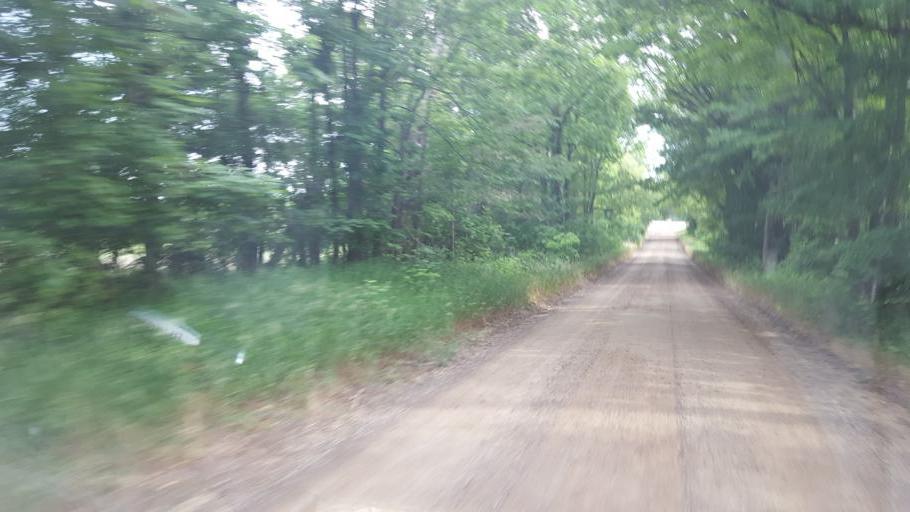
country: US
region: Michigan
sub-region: Eaton County
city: Charlotte
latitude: 42.6242
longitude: -84.8855
